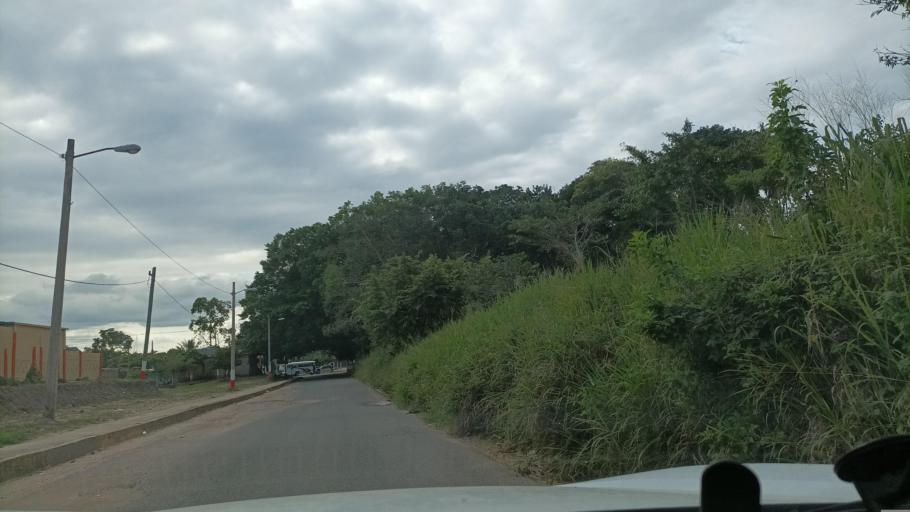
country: MX
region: Veracruz
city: Oluta
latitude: 17.9259
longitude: -94.8883
